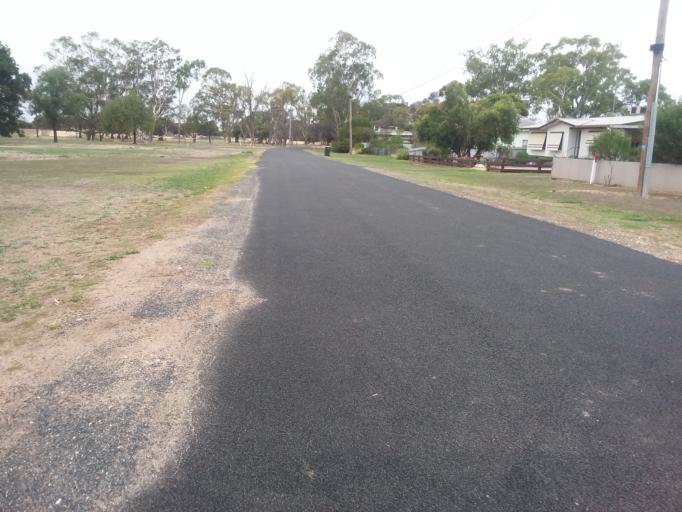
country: AU
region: Victoria
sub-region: Horsham
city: Horsham
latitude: -36.7407
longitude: 141.9383
